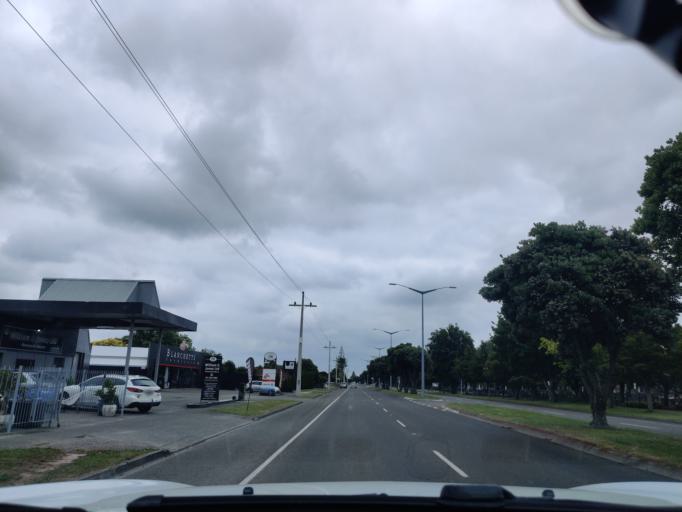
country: NZ
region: Manawatu-Wanganui
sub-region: Palmerston North City
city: Palmerston North
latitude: -40.3434
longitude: 175.6426
